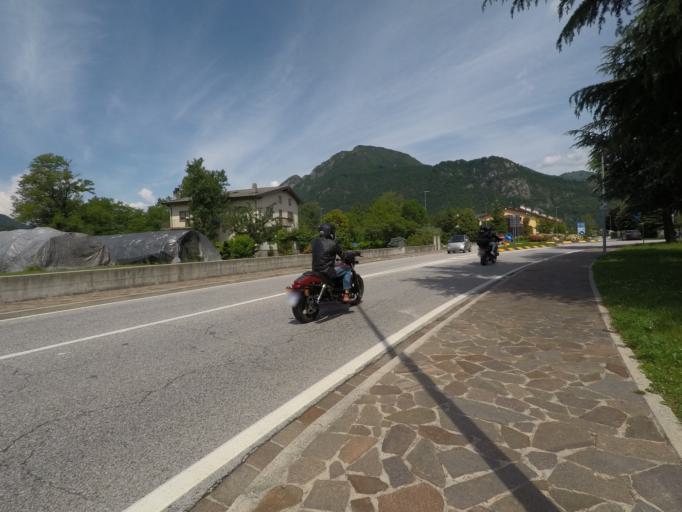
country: IT
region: Friuli Venezia Giulia
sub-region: Provincia di Udine
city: Tolmezzo
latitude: 46.4008
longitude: 13.0060
